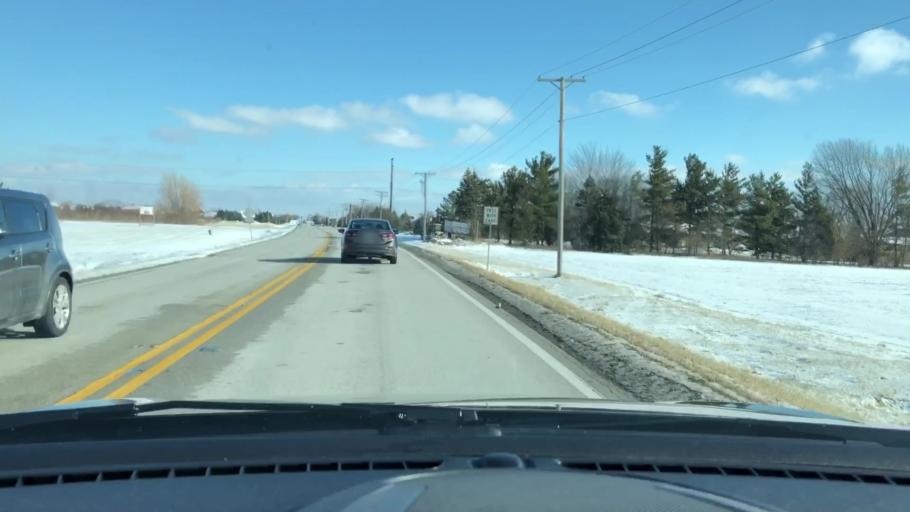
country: US
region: Illinois
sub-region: Will County
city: Mokena
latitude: 41.4837
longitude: -87.9053
